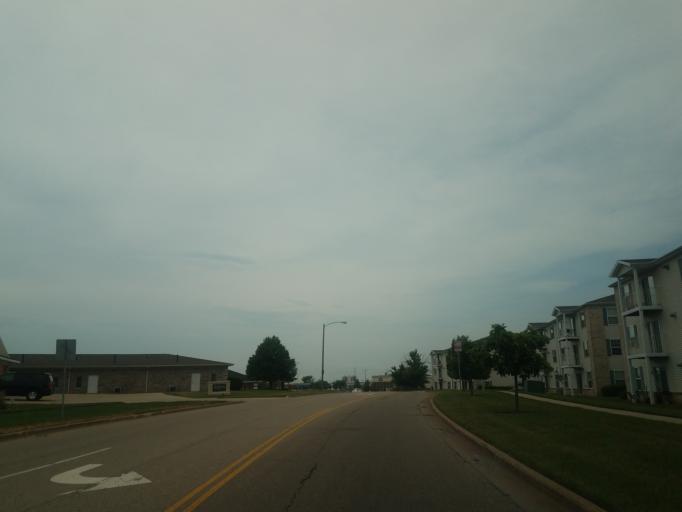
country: US
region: Illinois
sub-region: McLean County
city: Normal
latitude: 40.4963
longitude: -88.9478
